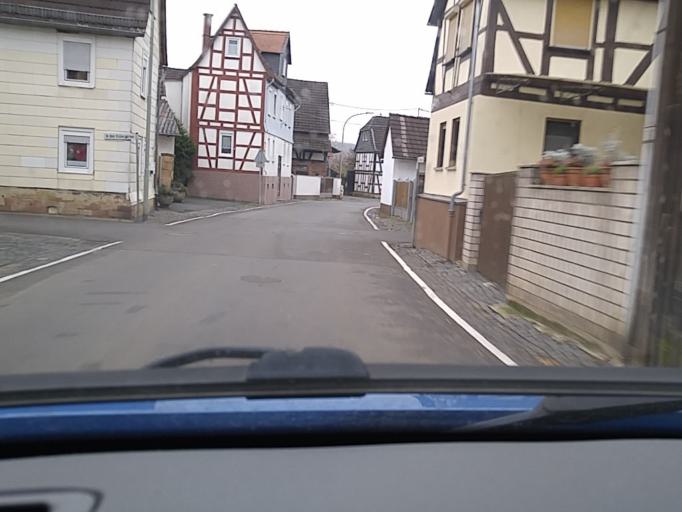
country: DE
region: Hesse
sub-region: Regierungsbezirk Darmstadt
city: Ranstadt
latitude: 50.3618
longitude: 8.9562
